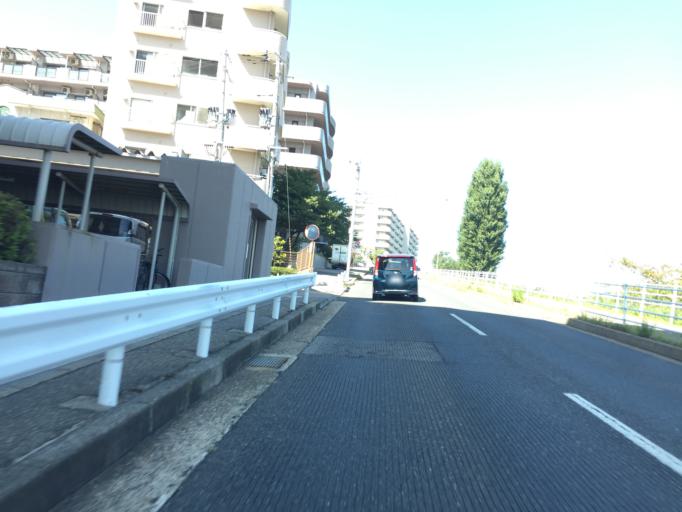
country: JP
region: Niigata
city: Niigata-shi
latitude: 37.8995
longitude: 139.0075
